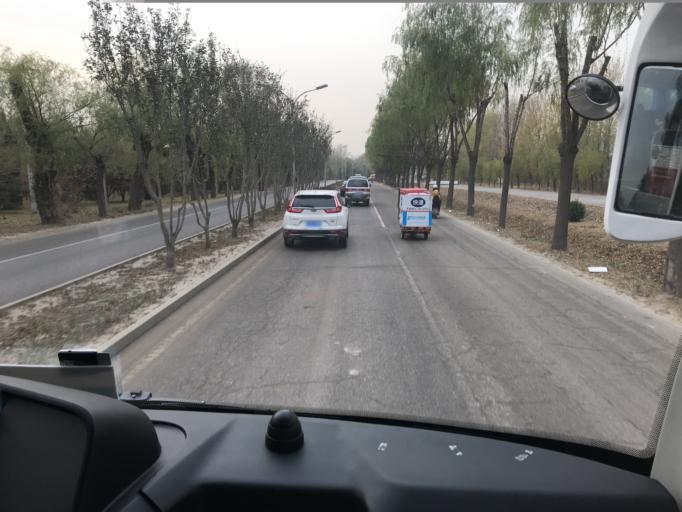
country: CN
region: Beijing
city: Wenquan
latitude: 40.0832
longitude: 116.2105
